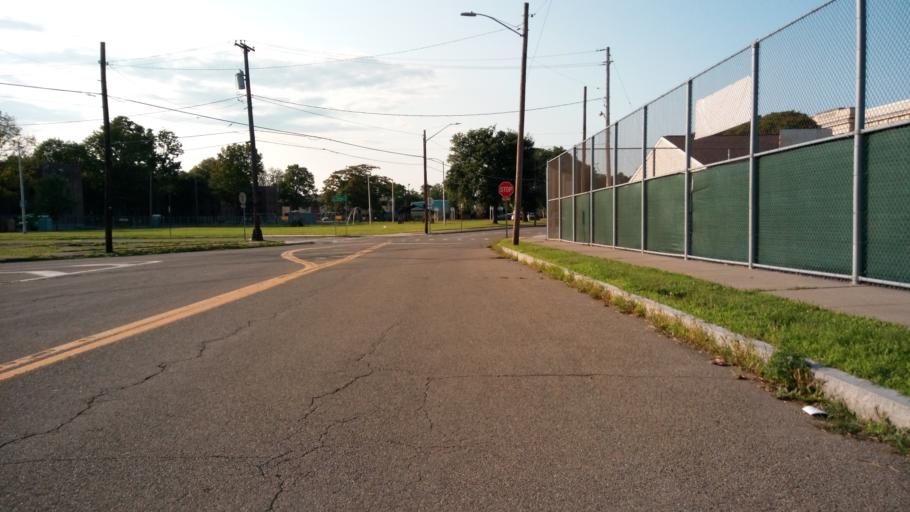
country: US
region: New York
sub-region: Chemung County
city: Elmira
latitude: 42.0949
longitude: -76.8044
